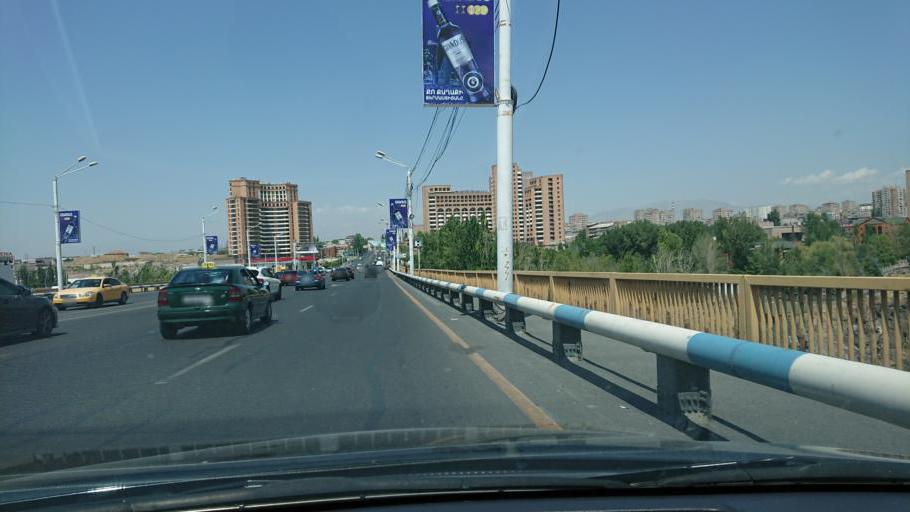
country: AM
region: Yerevan
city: Yerevan
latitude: 40.2102
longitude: 44.4930
